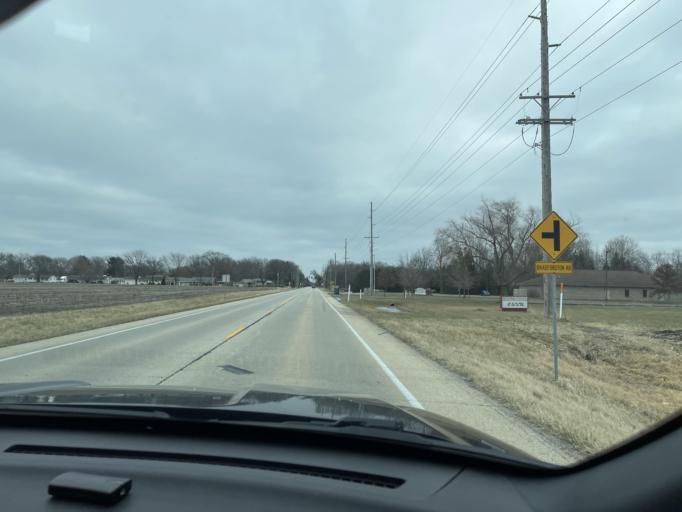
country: US
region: Illinois
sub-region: Sangamon County
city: Leland Grove
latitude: 39.7866
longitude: -89.7423
